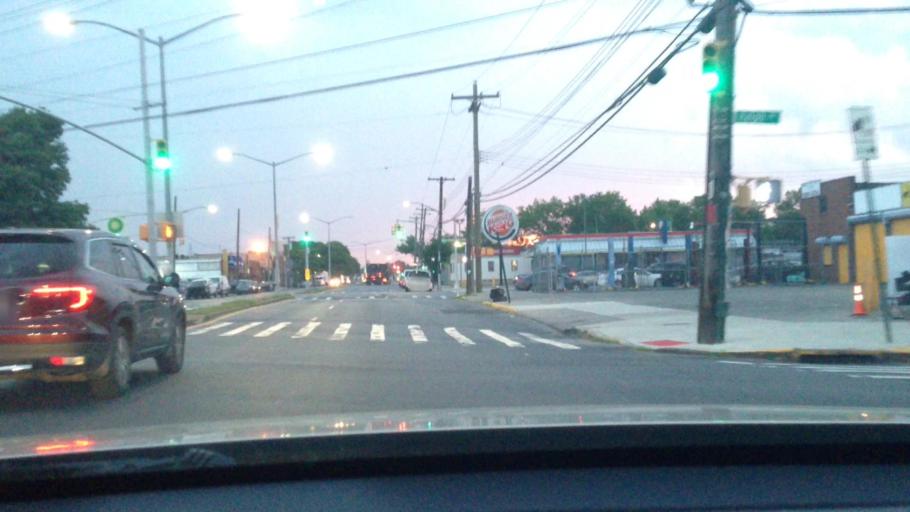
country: US
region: New York
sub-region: Kings County
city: Brooklyn
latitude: 40.6402
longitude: -73.9195
